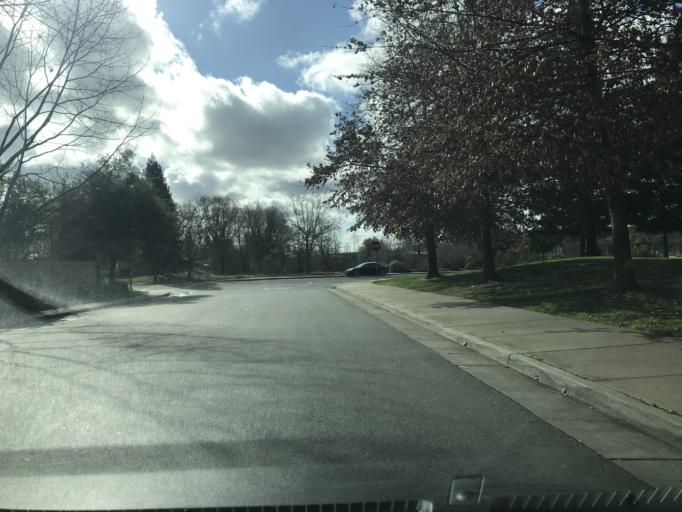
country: US
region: California
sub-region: Sacramento County
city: Folsom
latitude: 38.6520
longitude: -121.1344
